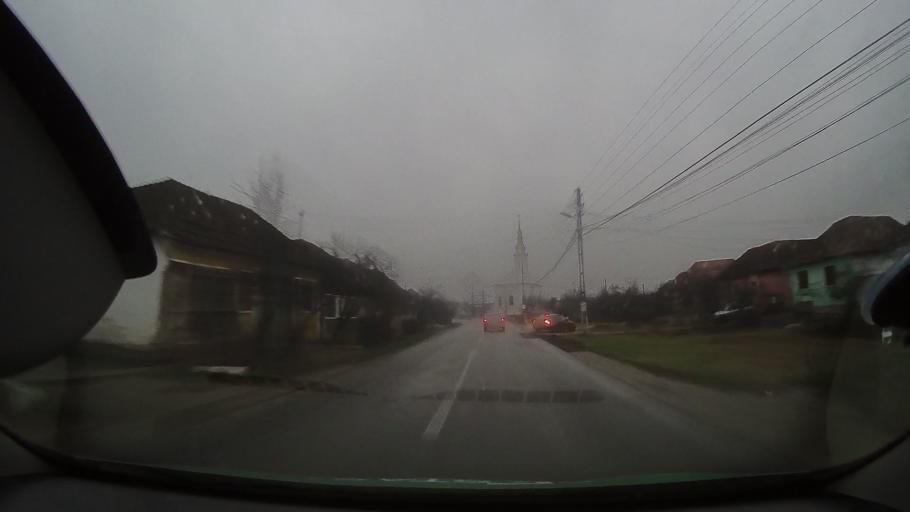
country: RO
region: Arad
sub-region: Comuna Craiova
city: Craiova
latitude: 46.5550
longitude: 21.9618
